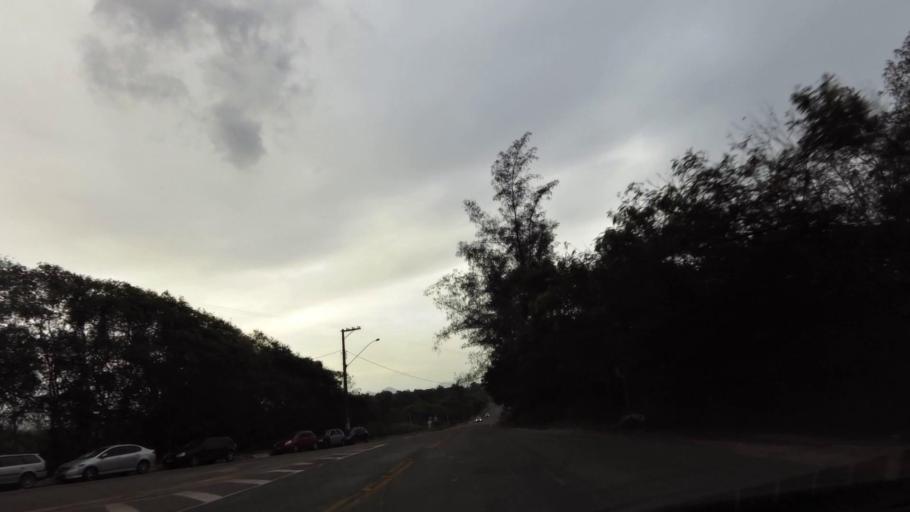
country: BR
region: Espirito Santo
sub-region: Guarapari
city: Guarapari
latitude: -20.7736
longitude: -40.5765
